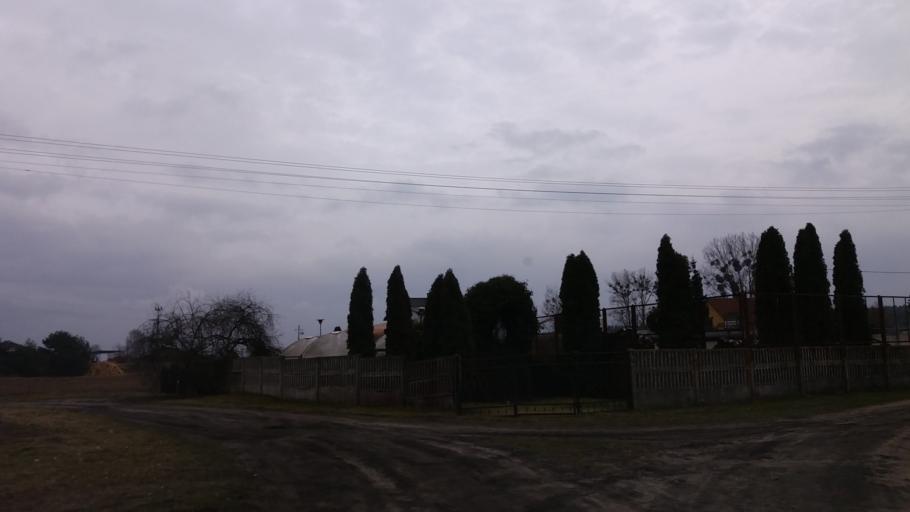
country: PL
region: West Pomeranian Voivodeship
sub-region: Powiat choszczenski
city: Drawno
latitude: 53.1441
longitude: 15.6816
